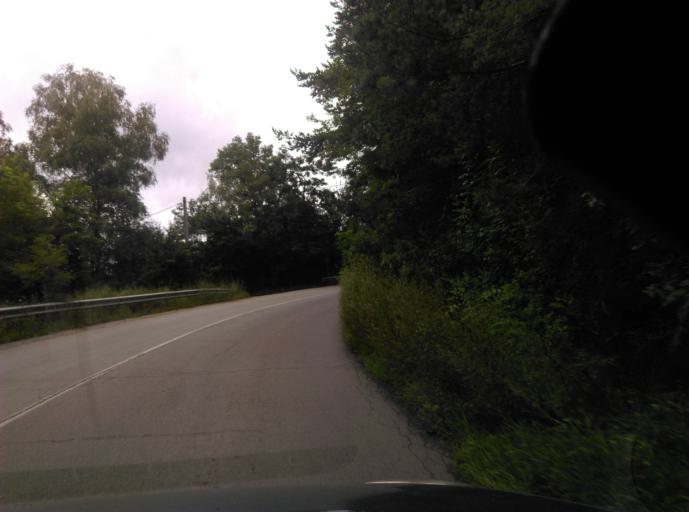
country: BG
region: Sofia-Capital
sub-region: Stolichna Obshtina
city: Sofia
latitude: 42.6051
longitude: 23.3513
